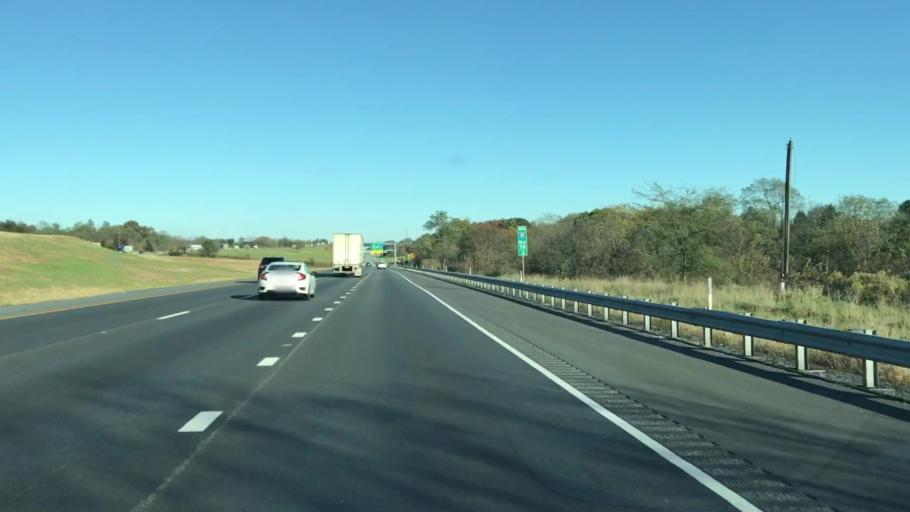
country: US
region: Pennsylvania
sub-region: Cumberland County
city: Mechanicsburg
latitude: 40.2732
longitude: -77.0126
